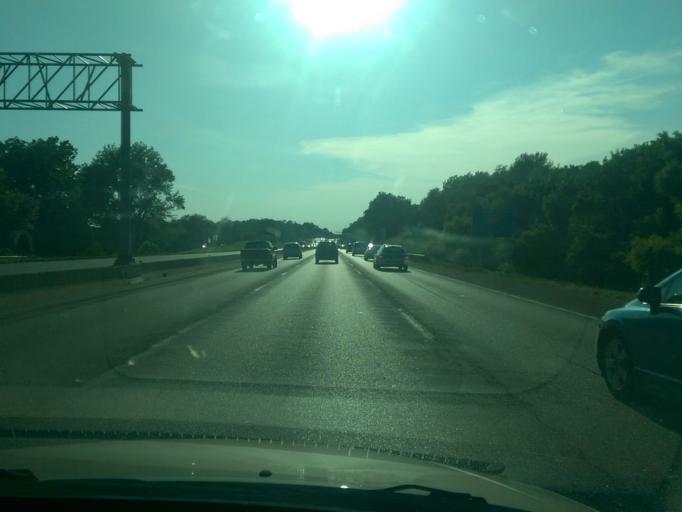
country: US
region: Missouri
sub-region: Jackson County
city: Raytown
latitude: 39.0476
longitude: -94.4530
